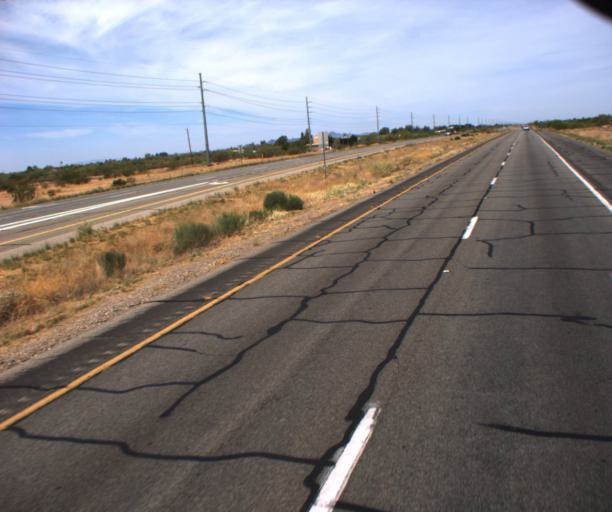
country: US
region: Arizona
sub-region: Maricopa County
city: Sun City West
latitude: 33.7672
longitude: -112.5147
